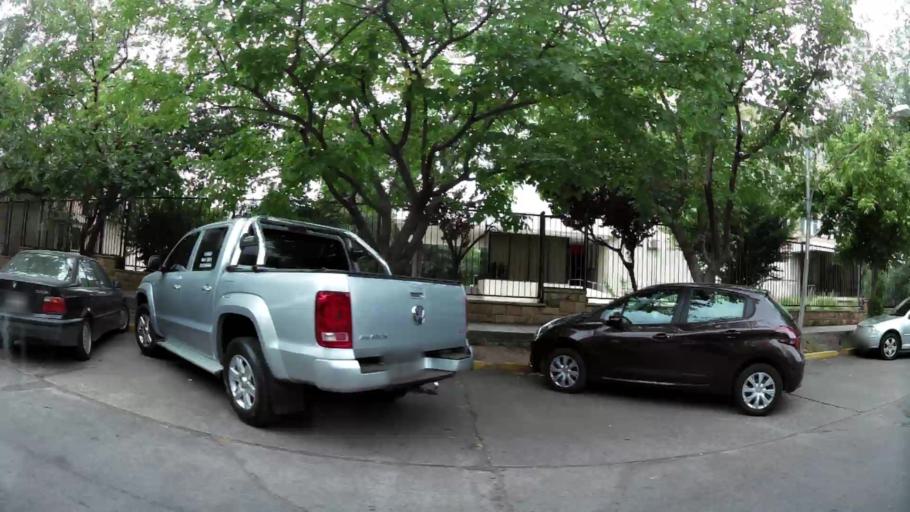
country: AR
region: Mendoza
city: Las Heras
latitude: -32.8672
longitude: -68.8547
